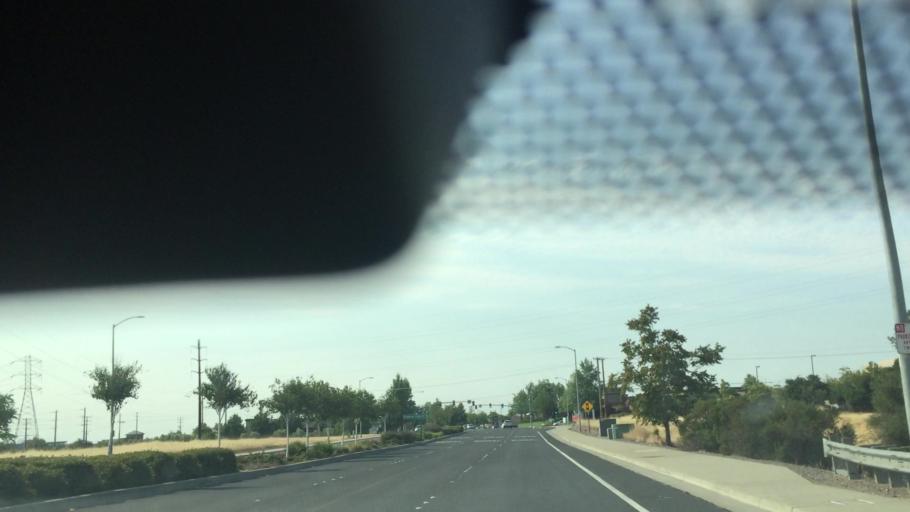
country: US
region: California
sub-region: Placer County
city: Roseville
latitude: 38.7652
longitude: -121.2612
